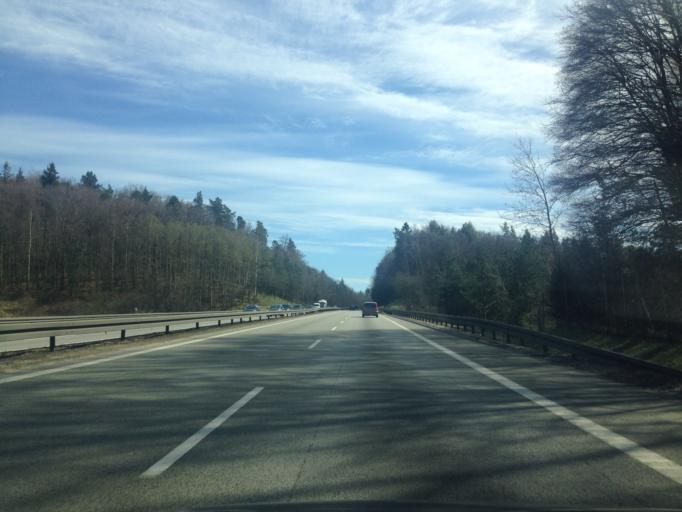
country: PL
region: Pomeranian Voivodeship
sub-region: Gdynia
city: Wielki Kack
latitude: 54.4571
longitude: 18.4898
